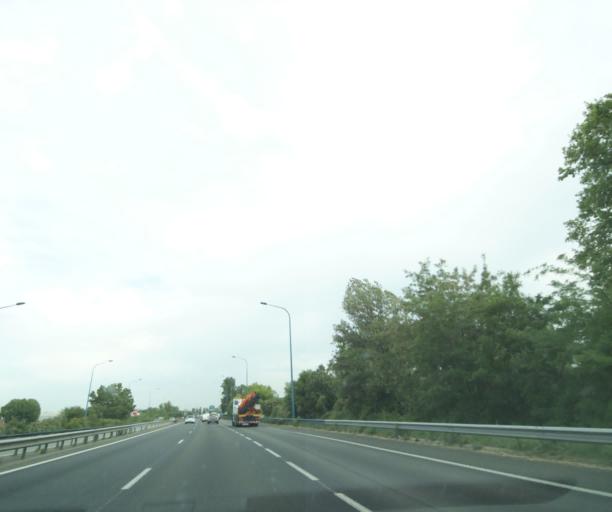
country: FR
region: Midi-Pyrenees
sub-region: Departement de la Haute-Garonne
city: Aucamville
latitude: 43.6418
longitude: 1.4218
